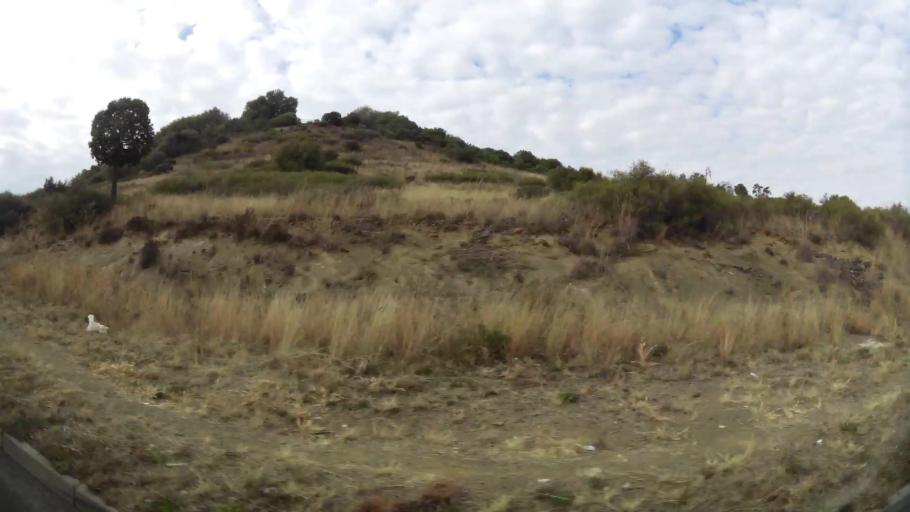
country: ZA
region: Orange Free State
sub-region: Mangaung Metropolitan Municipality
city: Bloemfontein
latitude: -29.1017
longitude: 26.2122
